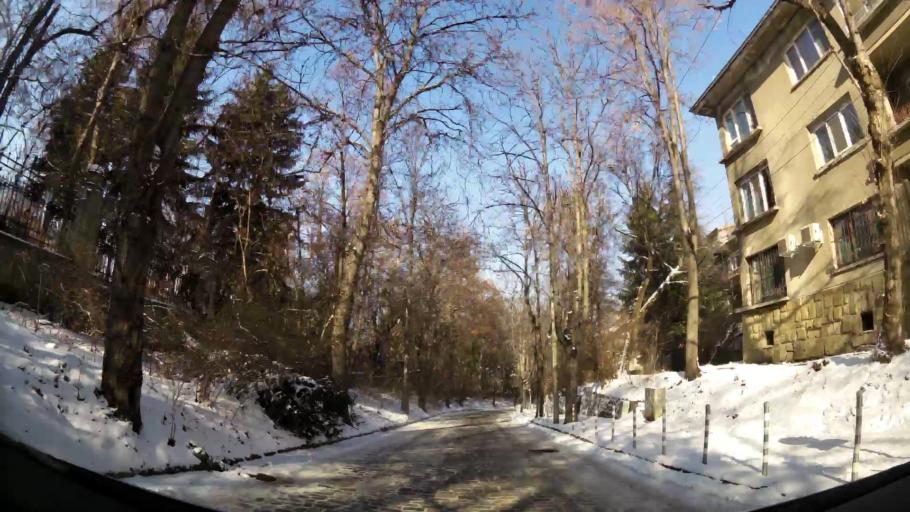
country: BG
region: Sofia-Capital
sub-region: Stolichna Obshtina
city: Sofia
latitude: 42.6758
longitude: 23.3272
